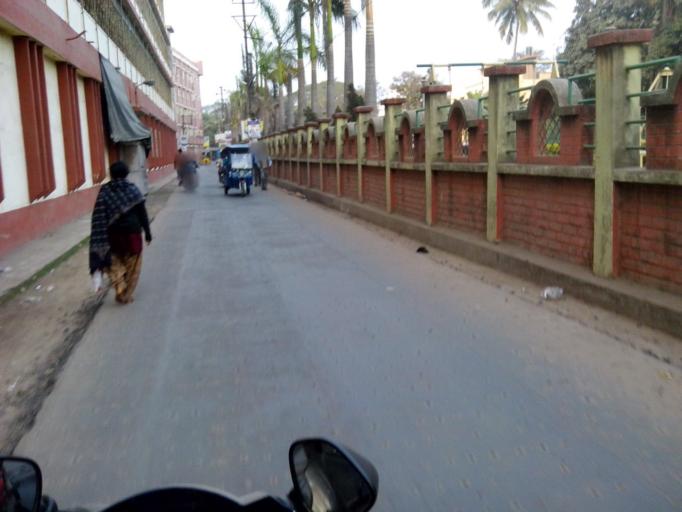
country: IN
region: West Bengal
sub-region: Barddhaman
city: Barddhaman
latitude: 23.2356
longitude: 87.8673
